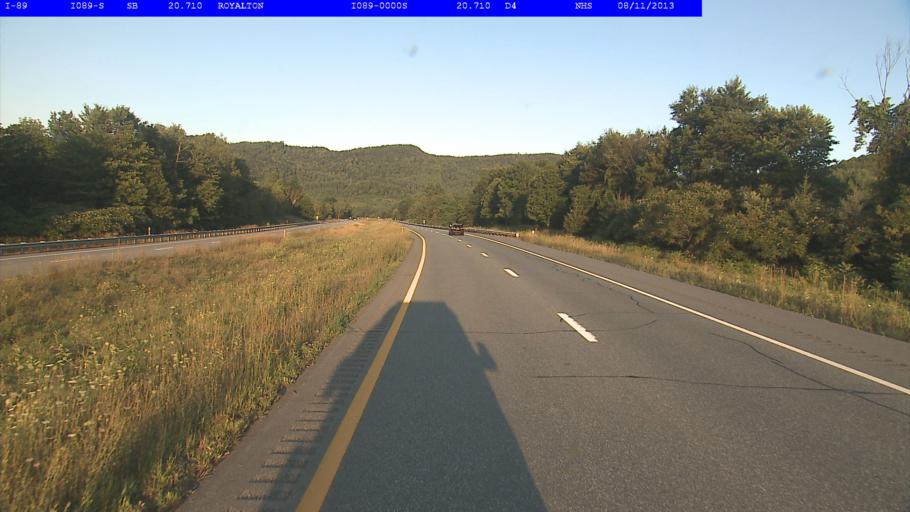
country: US
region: Vermont
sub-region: Orange County
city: Randolph
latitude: 43.8116
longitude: -72.5606
